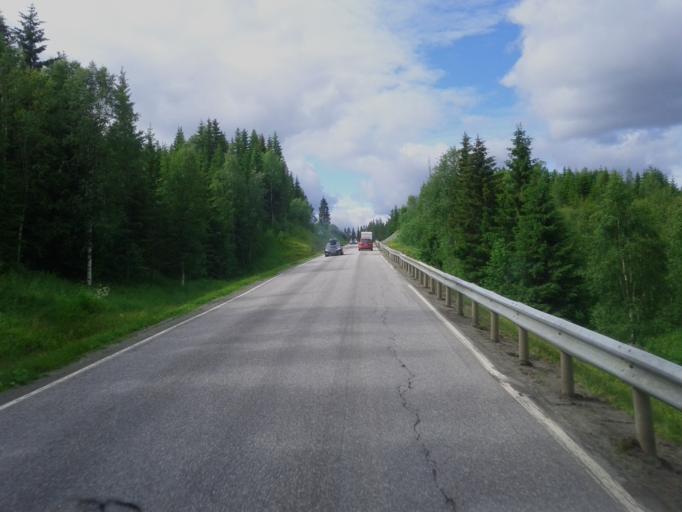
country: NO
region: Nord-Trondelag
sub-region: Hoylandet
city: Hoylandet
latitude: 64.6343
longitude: 12.6137
